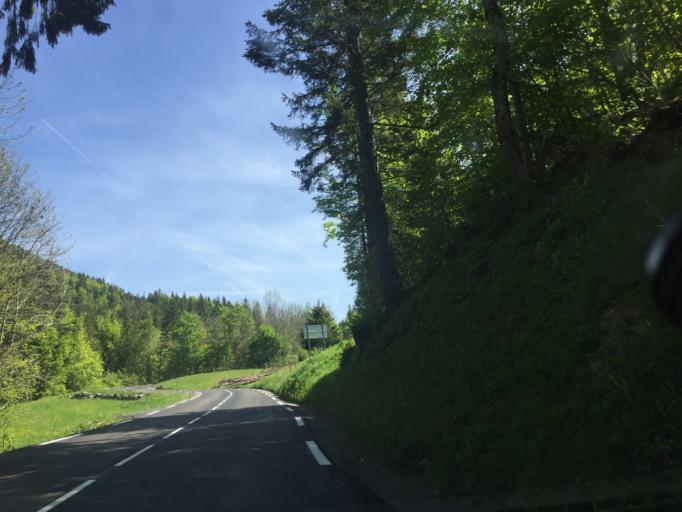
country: FR
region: Rhone-Alpes
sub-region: Departement de l'Isere
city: Saint-Hilaire
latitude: 45.3559
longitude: 5.8250
